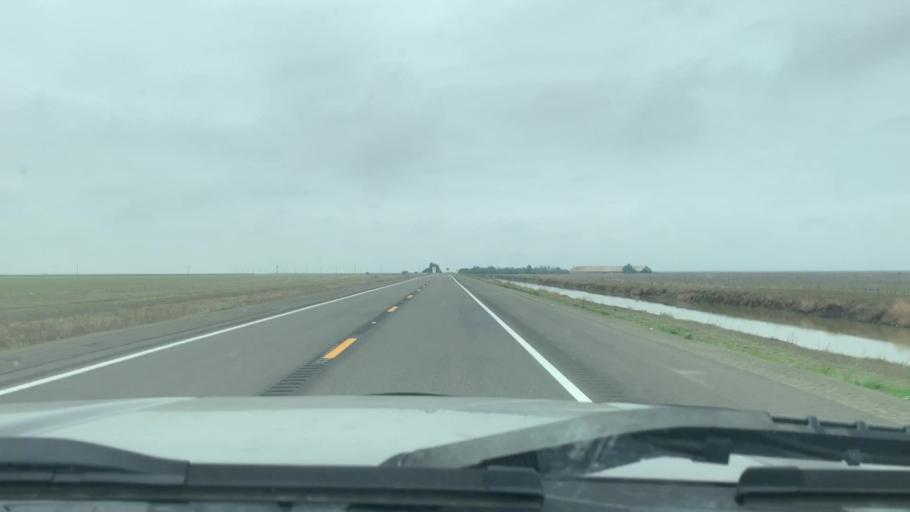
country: US
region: California
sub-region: Kings County
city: Kettleman City
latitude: 36.0440
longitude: -119.9514
